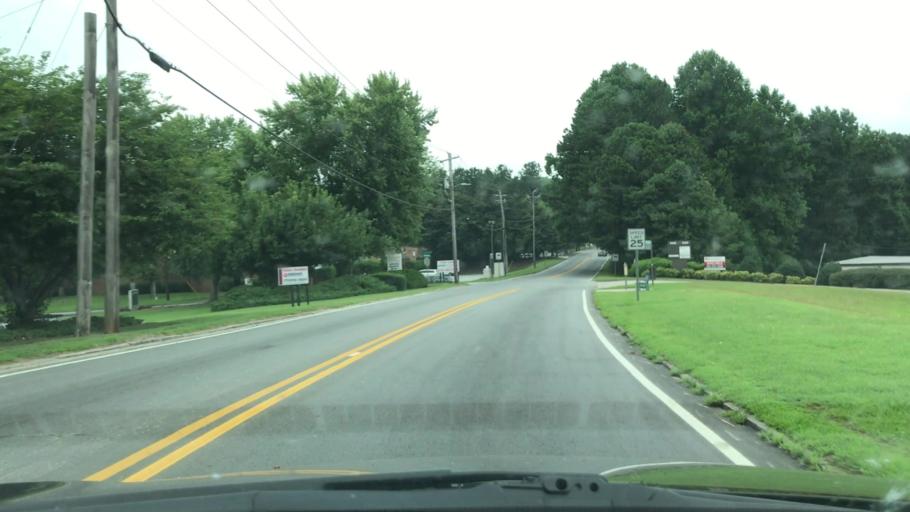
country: US
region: Georgia
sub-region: DeKalb County
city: Doraville
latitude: 33.9023
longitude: -84.2529
